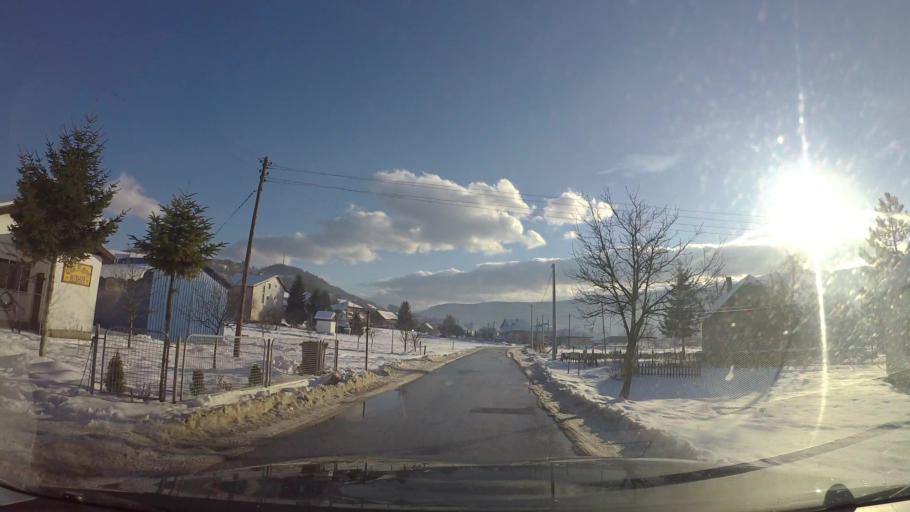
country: BA
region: Federation of Bosnia and Herzegovina
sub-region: Kanton Sarajevo
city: Sarajevo
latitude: 43.8114
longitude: 18.3461
